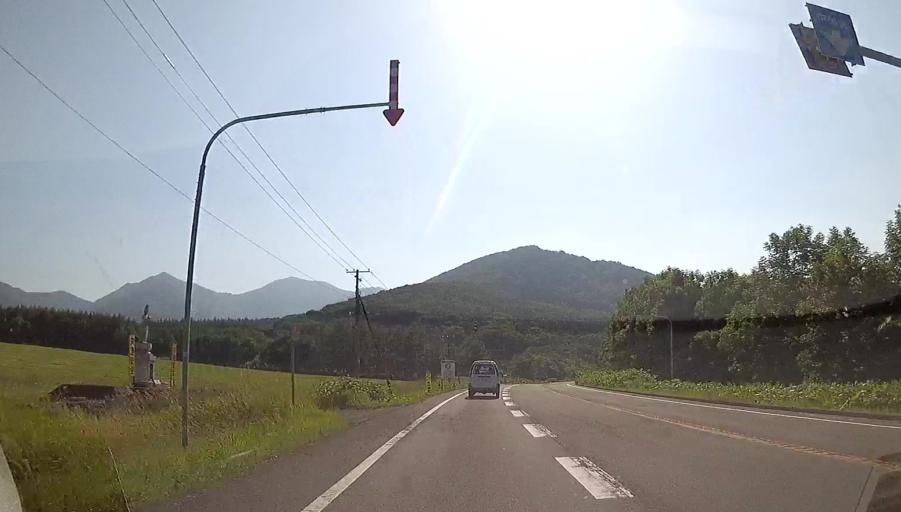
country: JP
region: Hokkaido
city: Otofuke
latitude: 42.9724
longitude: 142.8146
